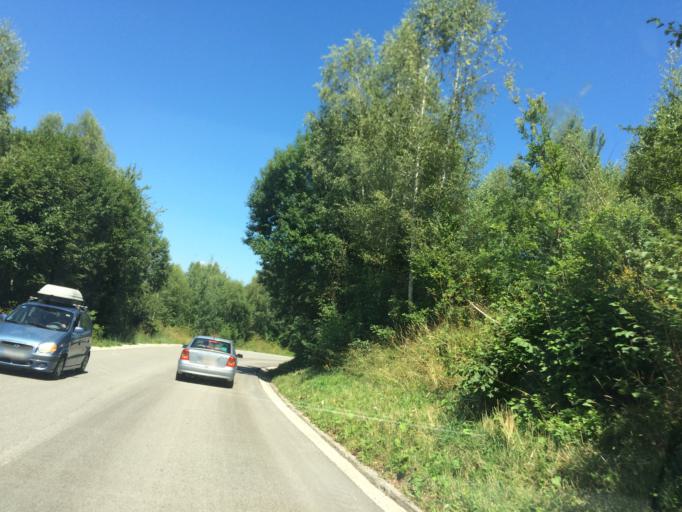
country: RS
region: Central Serbia
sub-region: Zlatiborski Okrug
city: Prijepolje
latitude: 43.3289
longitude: 19.5433
